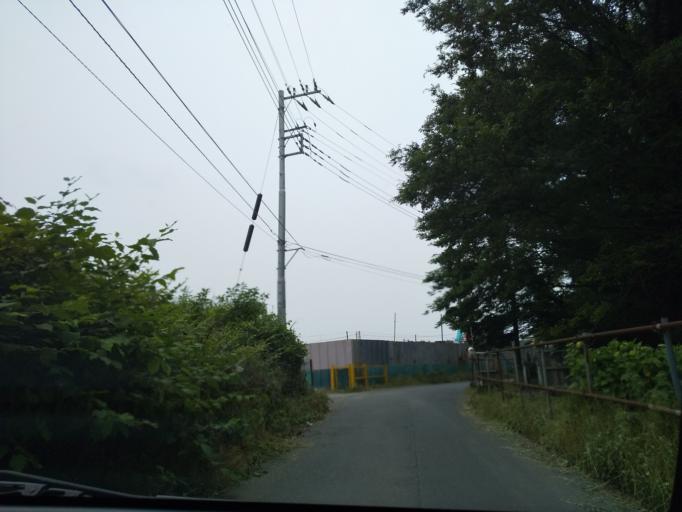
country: JP
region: Kanagawa
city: Zama
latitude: 35.5219
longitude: 139.3953
